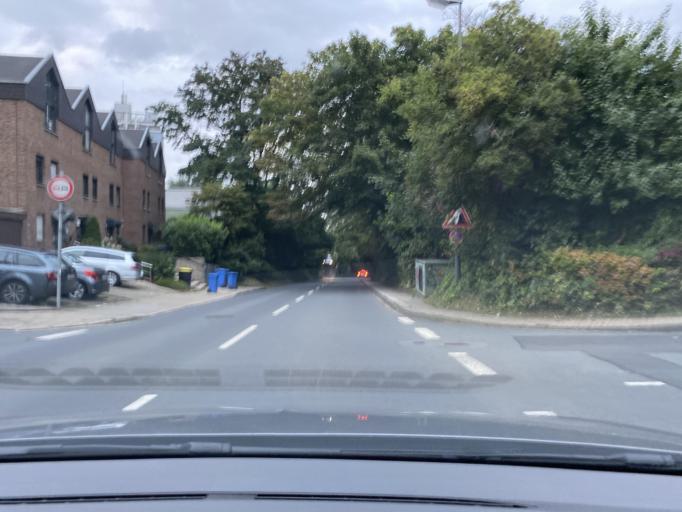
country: DE
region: North Rhine-Westphalia
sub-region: Regierungsbezirk Dusseldorf
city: Essen
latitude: 51.4361
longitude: 7.0776
